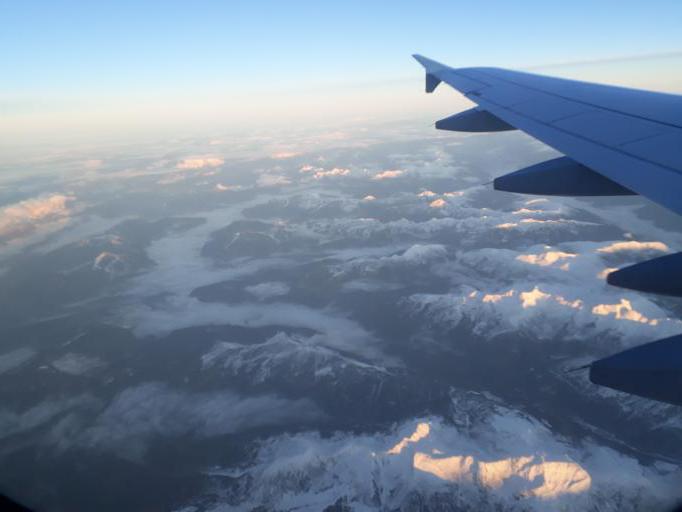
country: AT
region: Tyrol
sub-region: Politischer Bezirk Schwaz
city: Stummerberg
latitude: 47.3371
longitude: 11.9208
